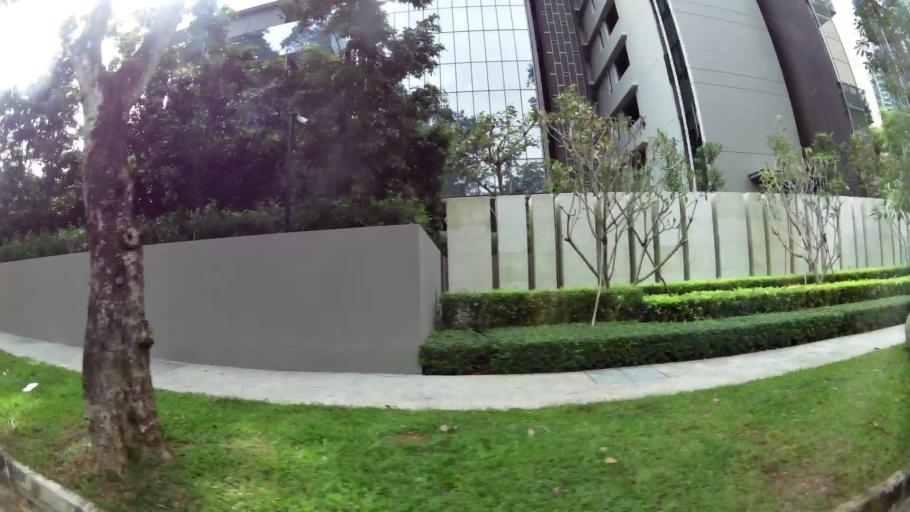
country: SG
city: Singapore
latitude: 1.3132
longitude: 103.8026
